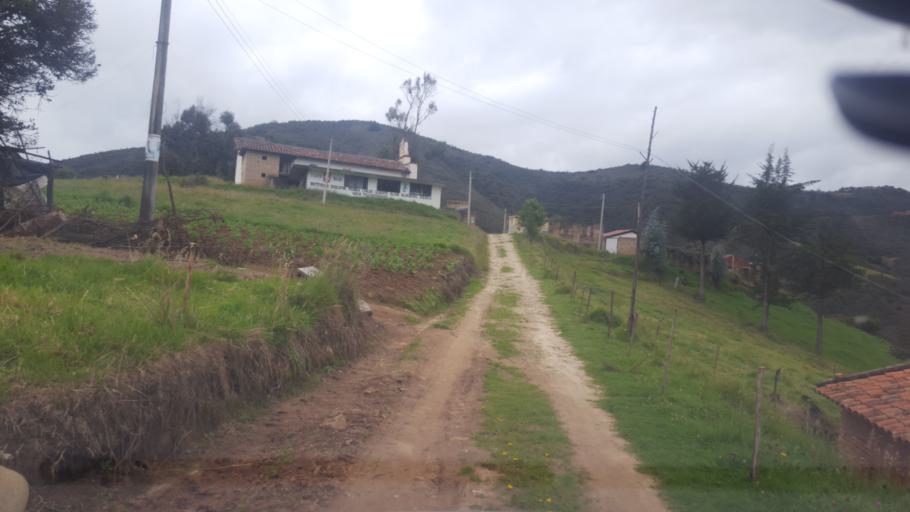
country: CO
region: Boyaca
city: Belen
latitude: 6.0159
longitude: -72.8770
